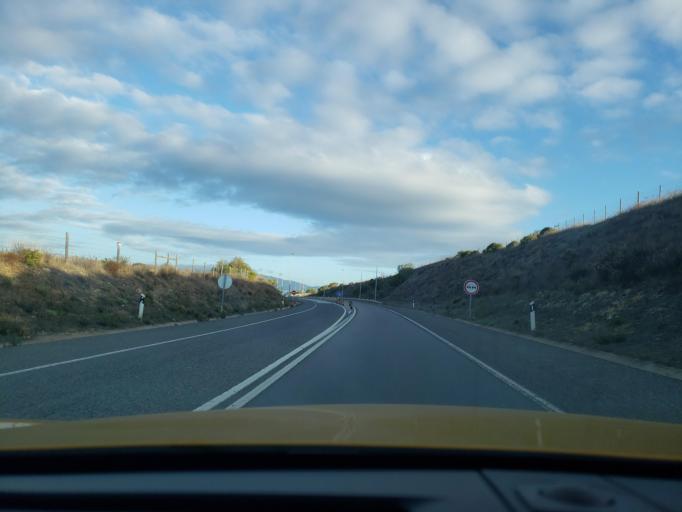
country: PT
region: Faro
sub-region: Portimao
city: Portimao
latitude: 37.1715
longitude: -8.5673
